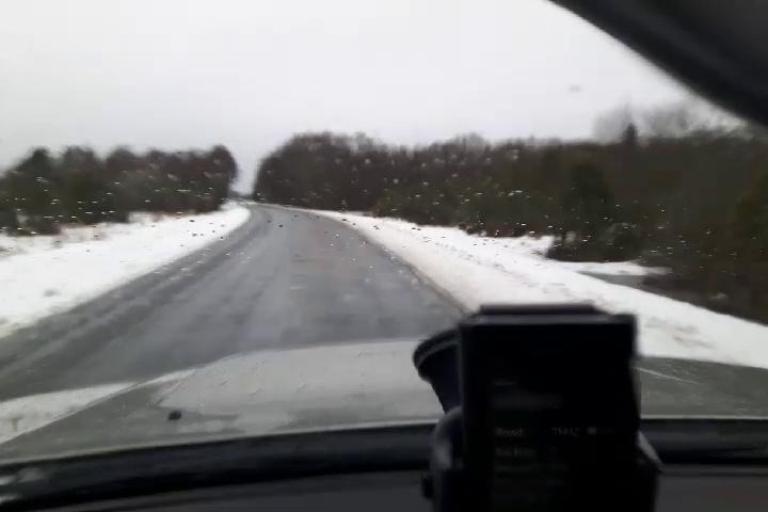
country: EE
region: Harju
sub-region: Harku vald
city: Tabasalu
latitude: 59.4275
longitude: 24.4283
